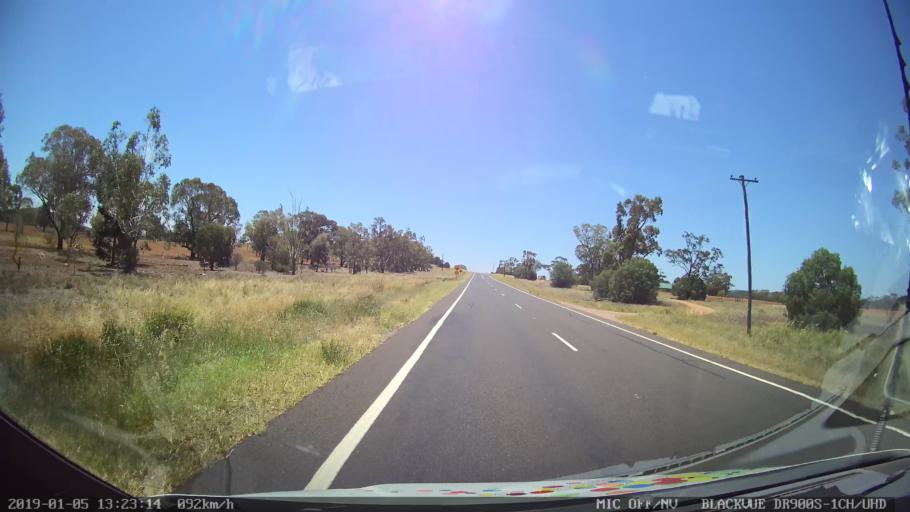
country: AU
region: New South Wales
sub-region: Gunnedah
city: Gunnedah
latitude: -31.0796
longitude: 149.9725
